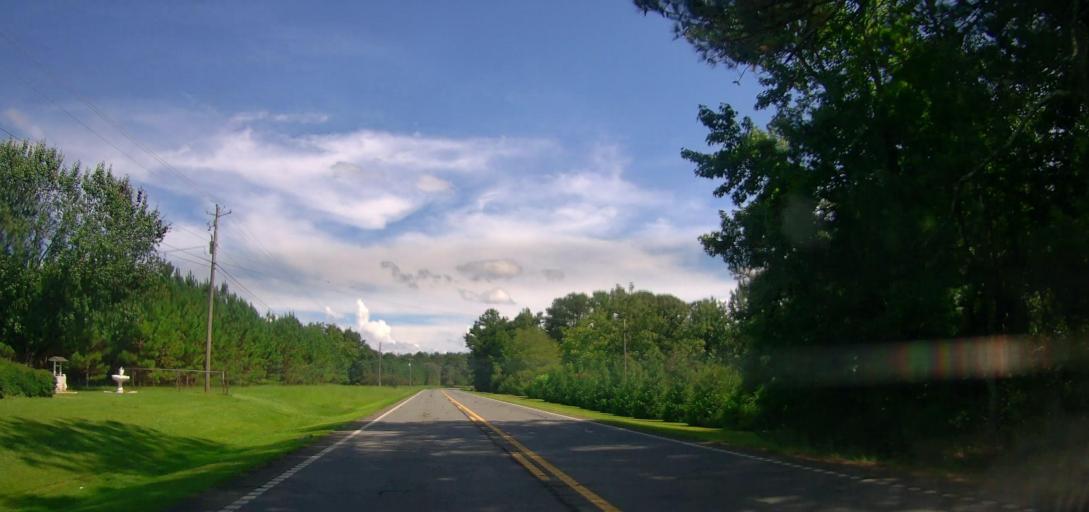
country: US
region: Georgia
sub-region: Talbot County
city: Sardis
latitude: 32.8177
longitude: -84.6045
